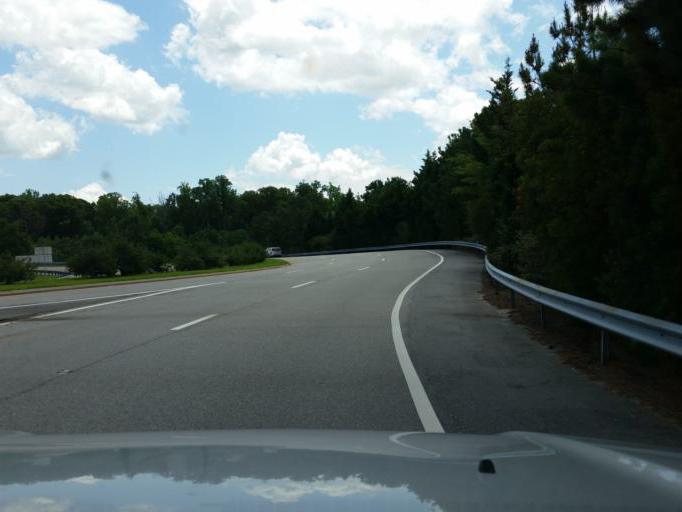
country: US
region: Virginia
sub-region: City of Williamsburg
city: Williamsburg
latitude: 37.2366
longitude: -76.6373
